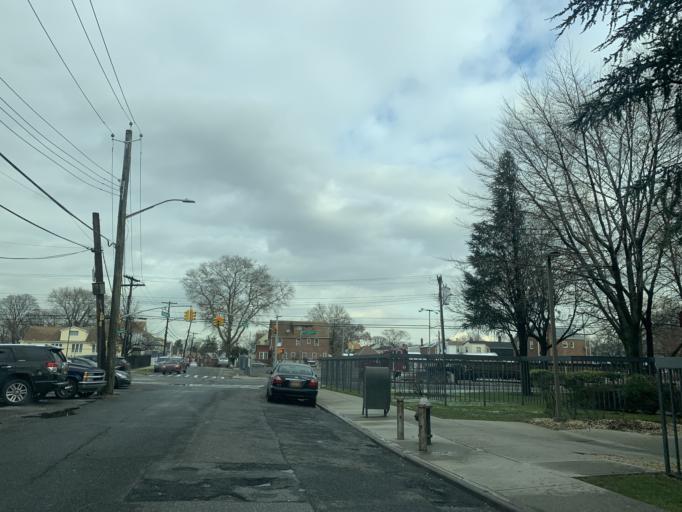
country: US
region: New York
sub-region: Queens County
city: Jamaica
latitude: 40.6911
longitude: -73.7879
